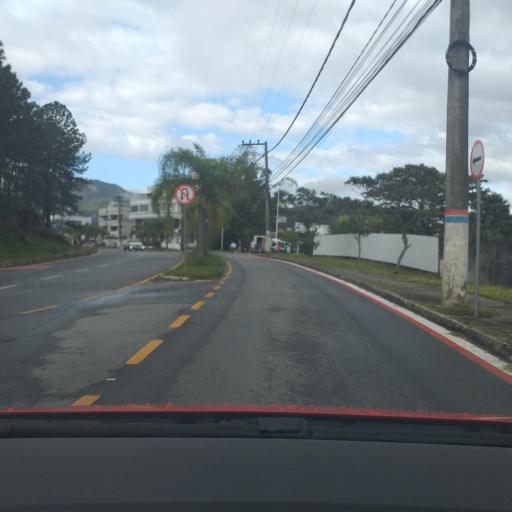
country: BR
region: Santa Catarina
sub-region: Florianopolis
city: Corrego Grande
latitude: -27.5960
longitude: -48.4982
